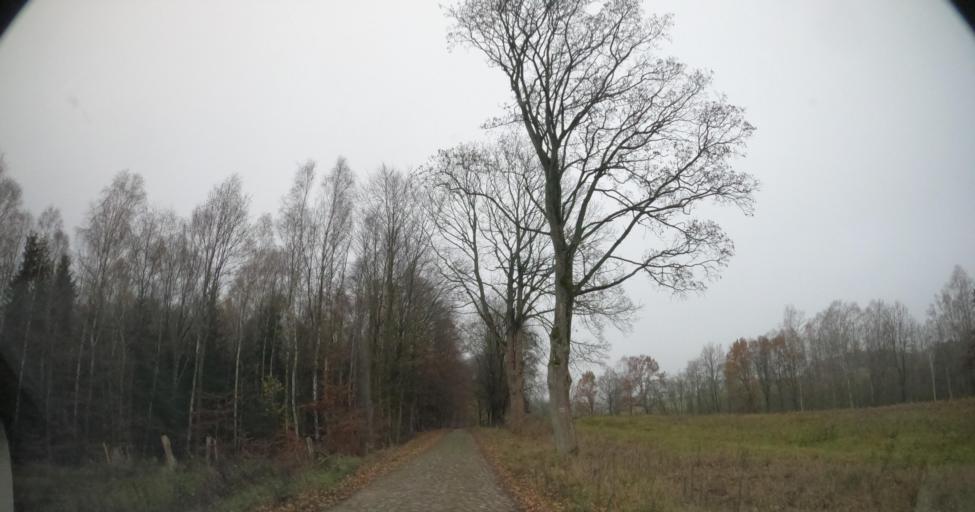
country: PL
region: West Pomeranian Voivodeship
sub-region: Powiat drawski
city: Drawsko Pomorskie
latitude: 53.5588
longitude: 15.7248
